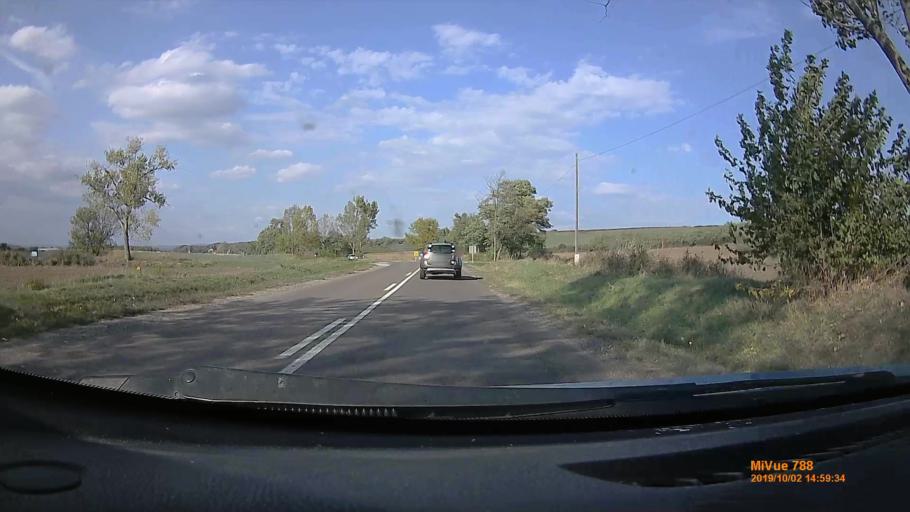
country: HU
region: Heves
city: Andornaktalya
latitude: 47.8260
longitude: 20.4193
